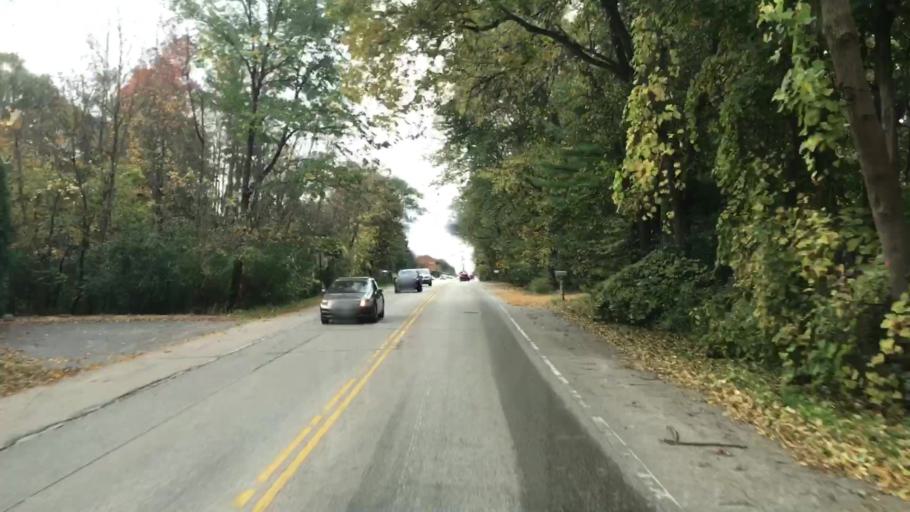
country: US
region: Wisconsin
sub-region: Waukesha County
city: Brookfield
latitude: 43.0641
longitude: -88.1260
